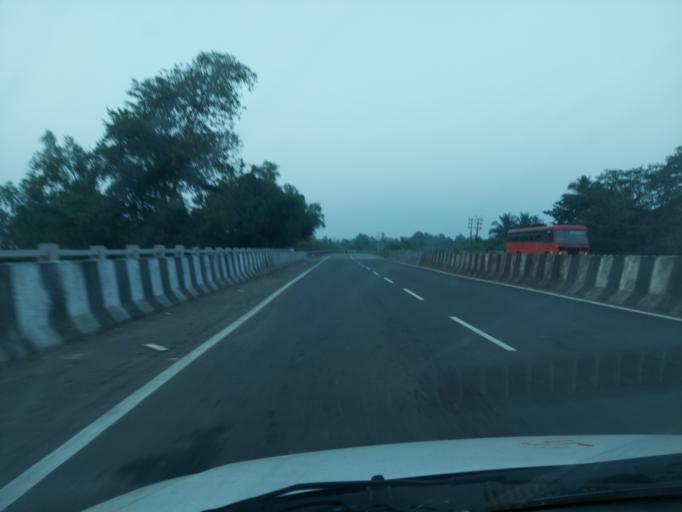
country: IN
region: Maharashtra
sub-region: Sindhudurg
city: Kudal
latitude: 16.0974
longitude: 73.7065
